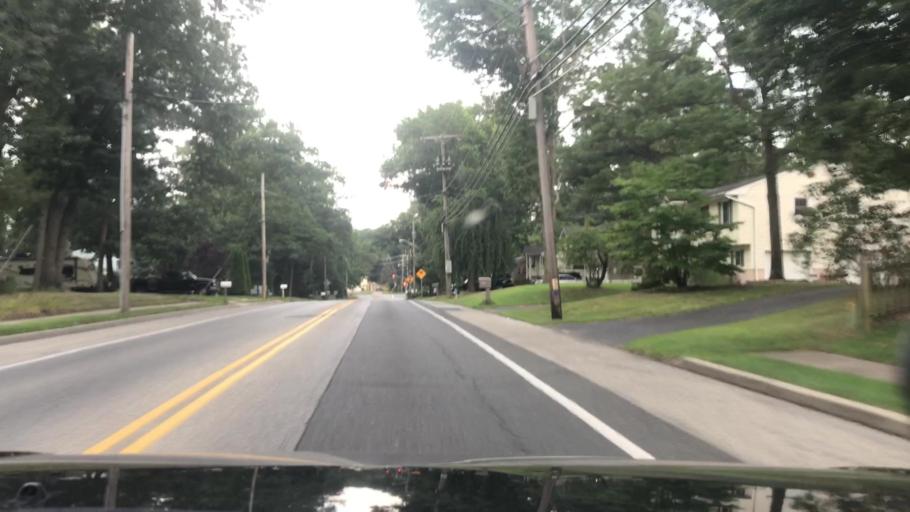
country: US
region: New Jersey
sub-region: Ocean County
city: Lakewood
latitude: 40.0918
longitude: -74.2697
